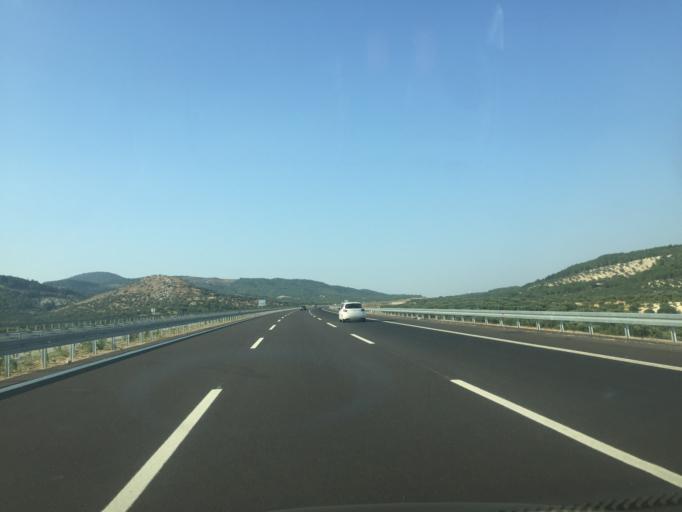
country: TR
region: Manisa
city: Zeytinliova
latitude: 38.9839
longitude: 27.7316
